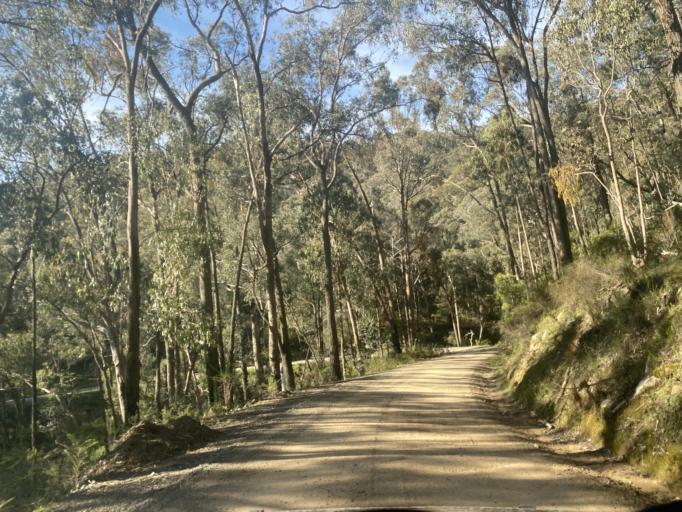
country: AU
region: Victoria
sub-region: Mansfield
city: Mansfield
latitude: -36.8300
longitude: 146.1650
